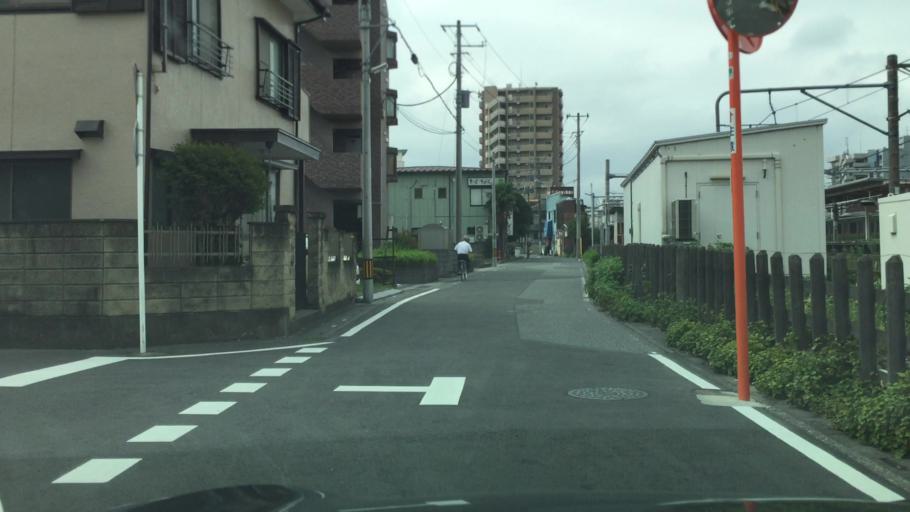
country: JP
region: Saitama
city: Ageoshimo
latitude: 35.9428
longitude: 139.6091
